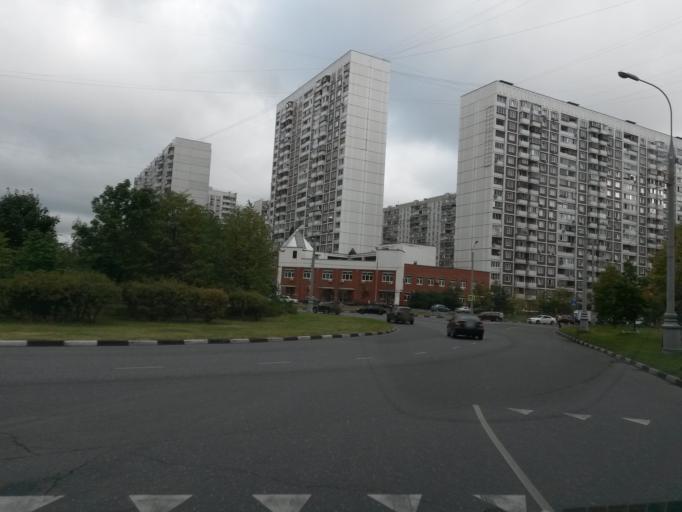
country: RU
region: Moscow
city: Brateyevo
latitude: 55.6557
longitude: 37.7630
